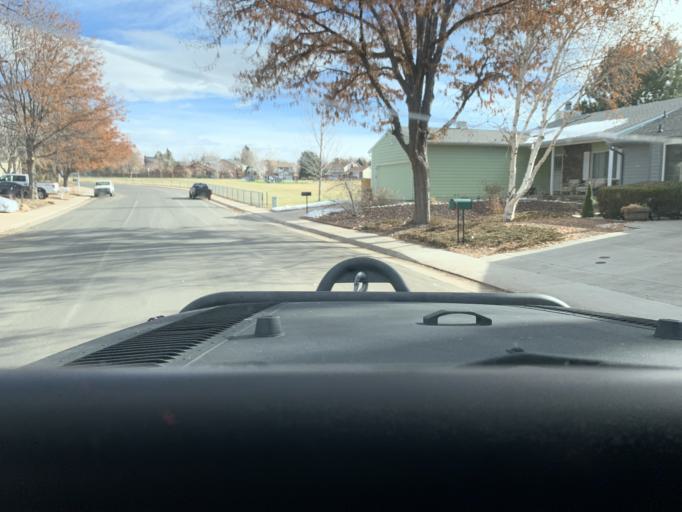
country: US
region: Colorado
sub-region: Adams County
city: Aurora
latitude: 39.7037
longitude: -104.8036
